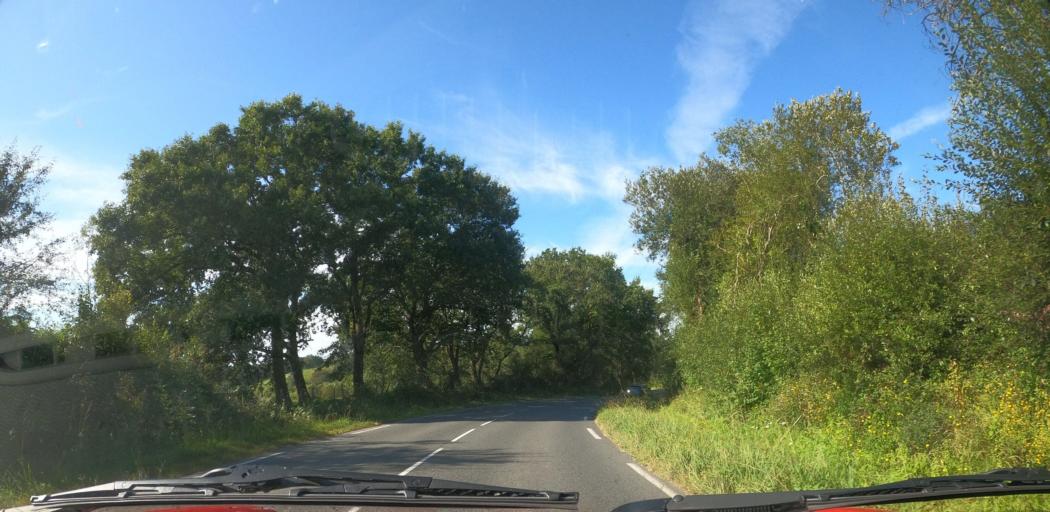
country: FR
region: Aquitaine
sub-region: Departement des Pyrenees-Atlantiques
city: Saint-Pee-sur-Nivelle
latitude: 43.3911
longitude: -1.5343
